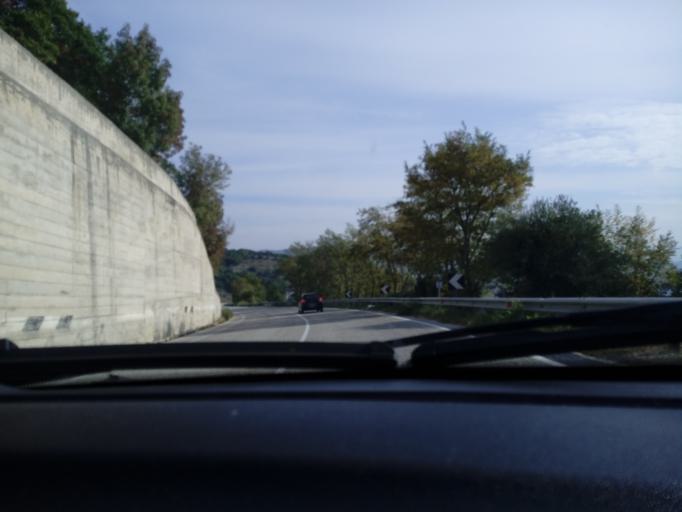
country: IT
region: Molise
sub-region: Provincia di Campobasso
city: Gambatesa
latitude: 41.5246
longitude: 14.8643
